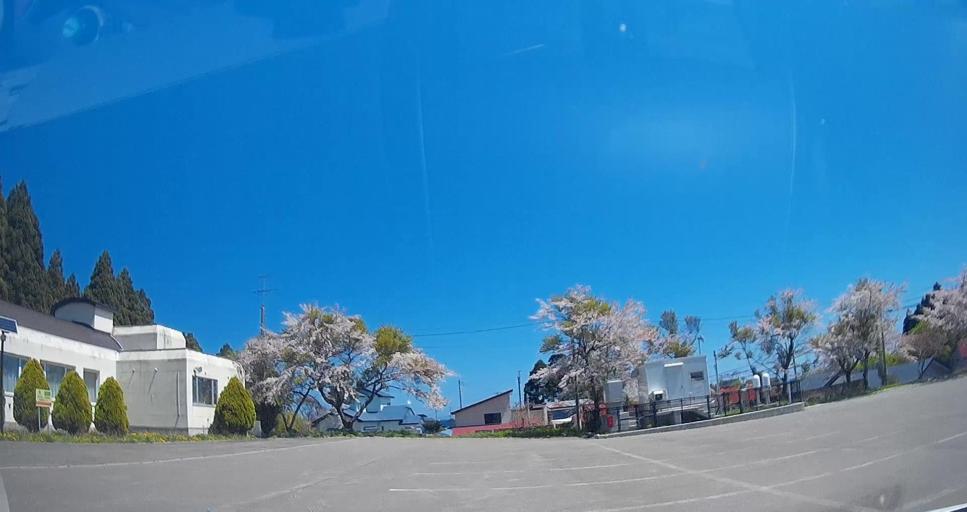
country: JP
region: Aomori
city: Mutsu
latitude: 41.3705
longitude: 141.4446
